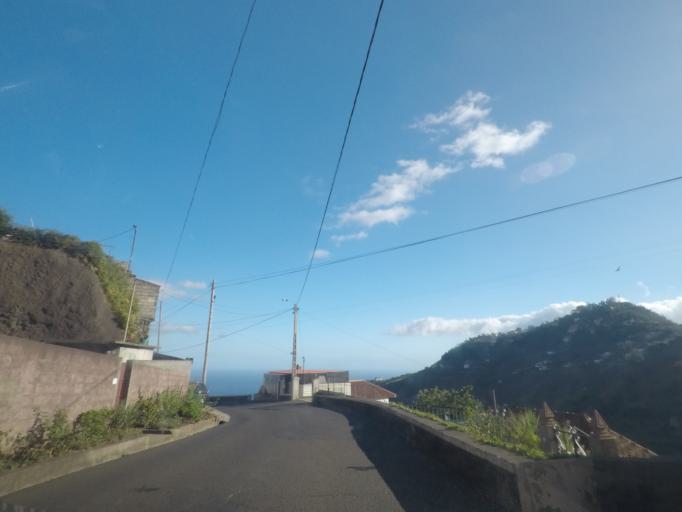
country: PT
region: Madeira
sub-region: Ribeira Brava
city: Campanario
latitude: 32.6663
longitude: -16.9983
